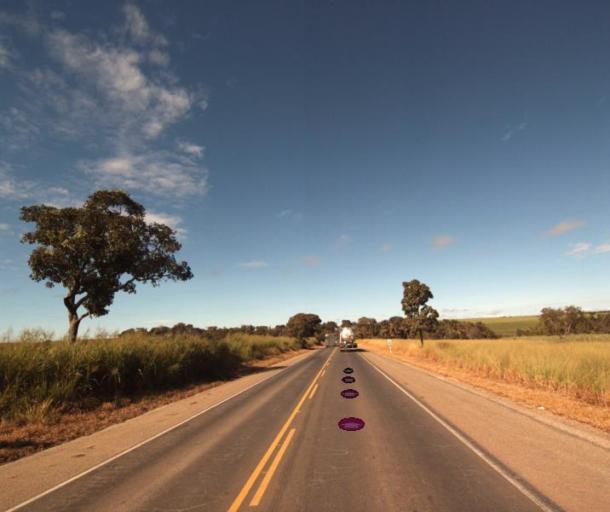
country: BR
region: Goias
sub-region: Itapaci
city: Itapaci
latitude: -14.8391
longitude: -49.3095
